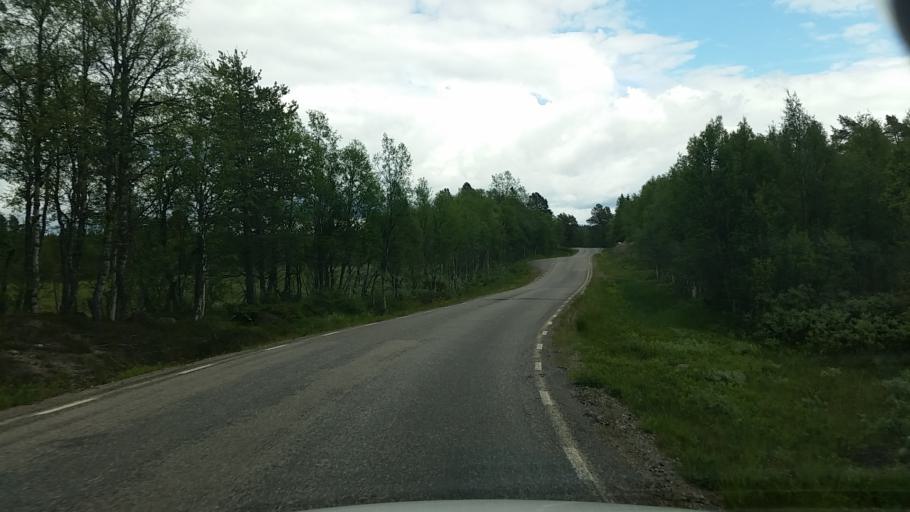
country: NO
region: Hedmark
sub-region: Engerdal
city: Engerdal
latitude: 62.1495
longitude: 12.9814
